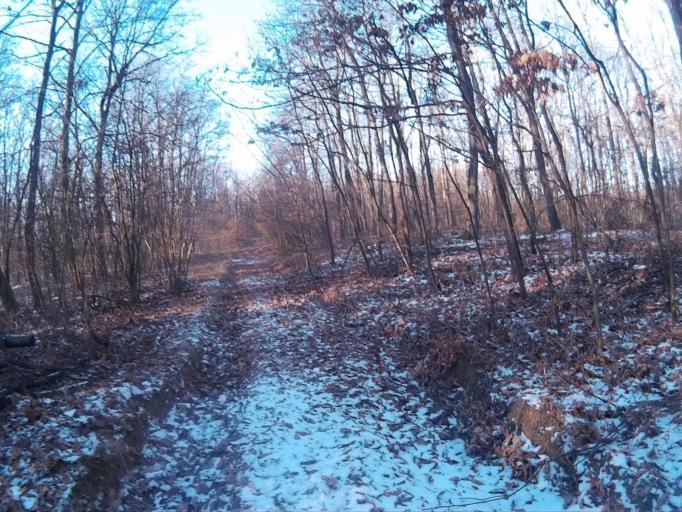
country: HU
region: Borsod-Abauj-Zemplen
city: Putnok
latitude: 48.4631
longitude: 20.4651
